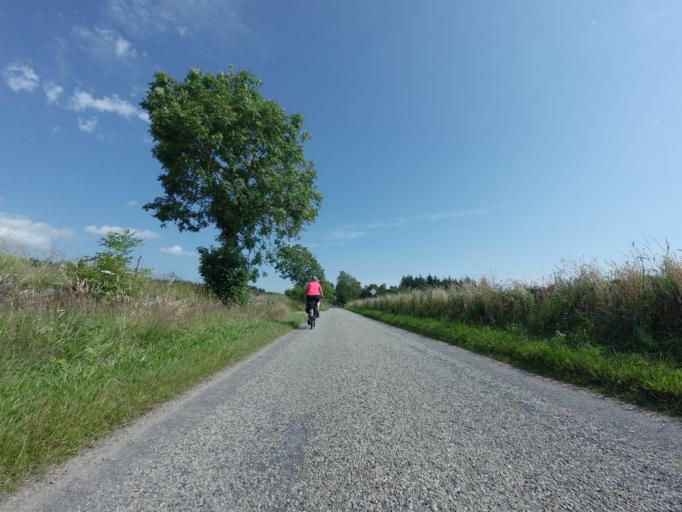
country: GB
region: Scotland
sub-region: Highland
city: Invergordon
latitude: 57.7258
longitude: -4.1969
